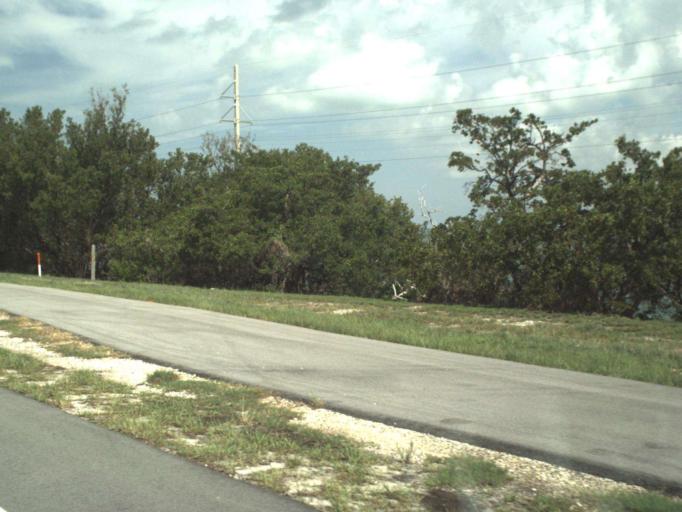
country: US
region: Florida
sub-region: Monroe County
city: Islamorada
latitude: 24.8404
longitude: -80.7838
